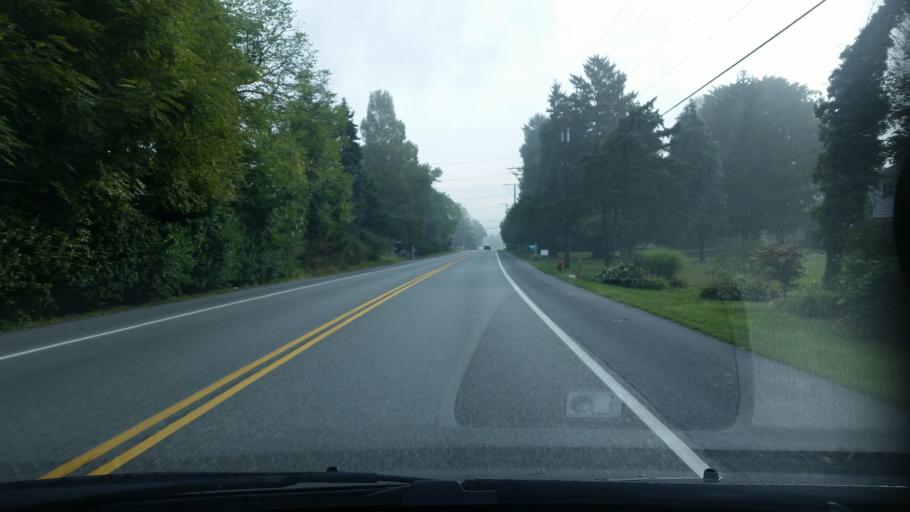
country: US
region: Pennsylvania
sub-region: Lancaster County
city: Brownstown
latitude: 40.0805
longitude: -76.2469
